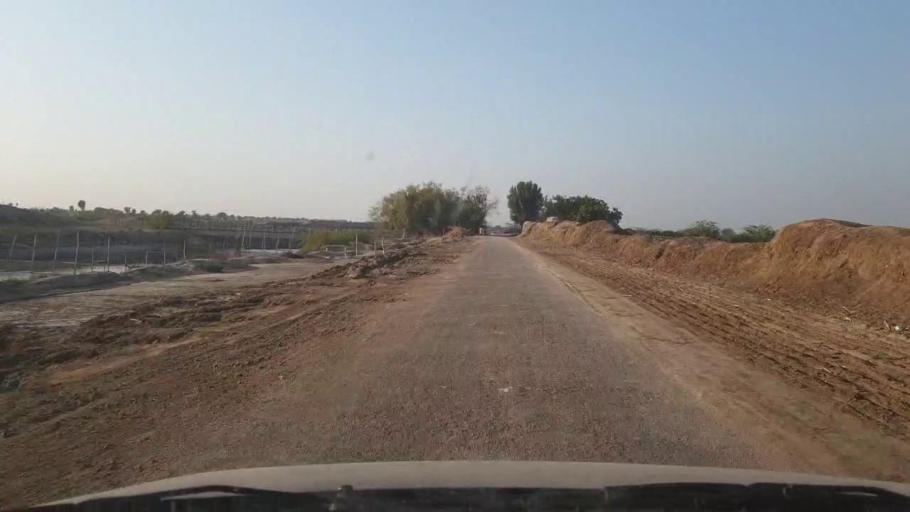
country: PK
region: Sindh
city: Samaro
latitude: 25.2897
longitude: 69.3337
